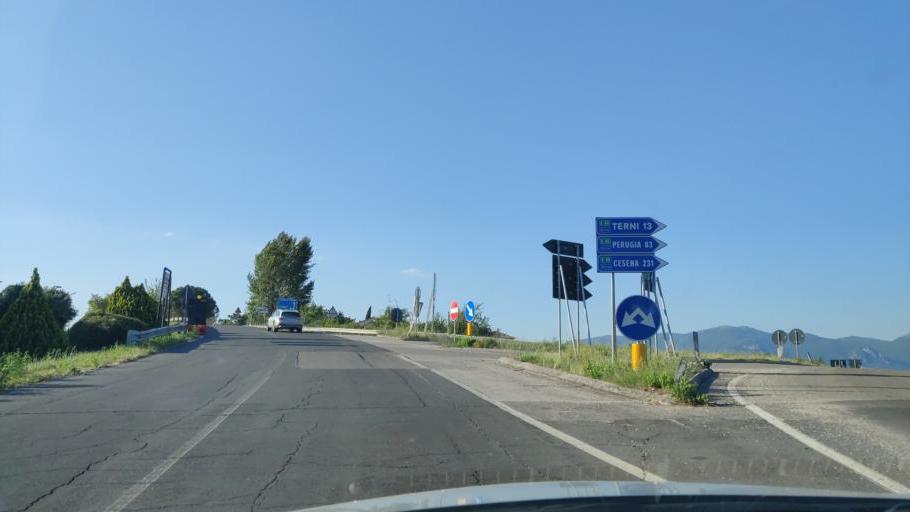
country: IT
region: Umbria
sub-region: Provincia di Terni
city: Narni Scalo
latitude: 42.5396
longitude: 12.5143
